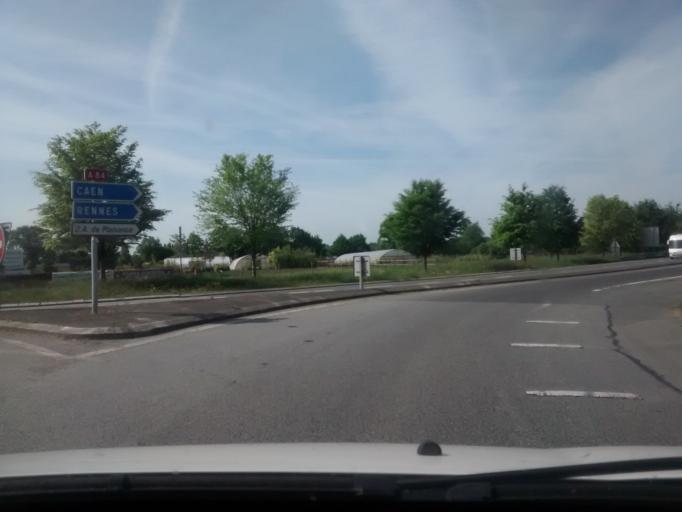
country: FR
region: Brittany
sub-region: Departement d'Ille-et-Vilaine
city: Romagne
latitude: 48.3426
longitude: -1.2928
